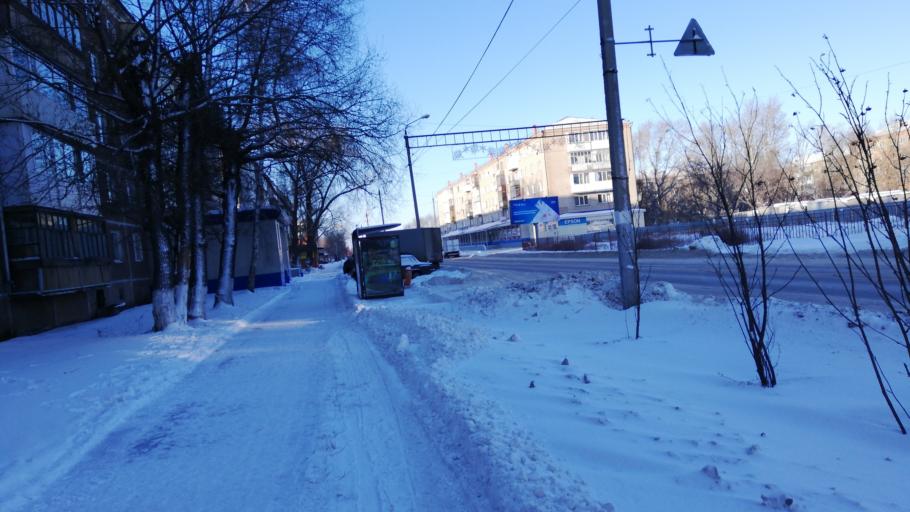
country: KZ
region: Soltustik Qazaqstan
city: Petropavlovsk
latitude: 54.8606
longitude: 69.1501
